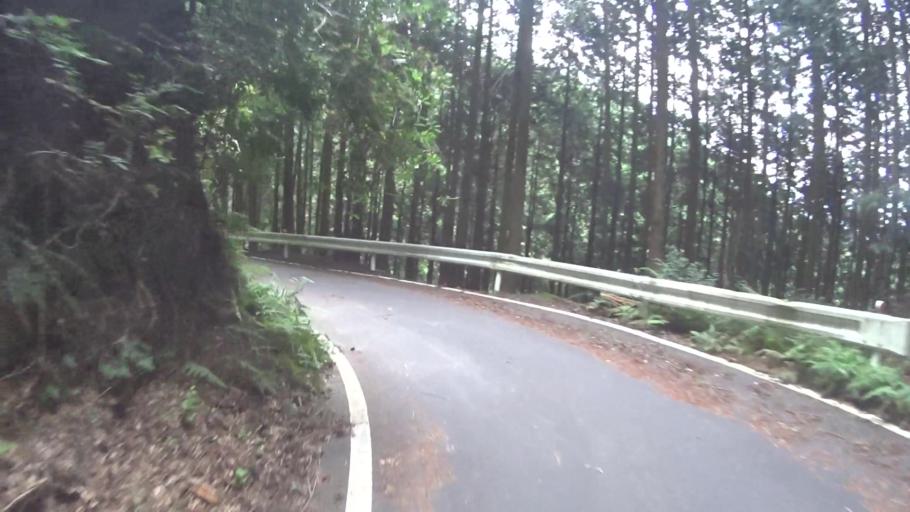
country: JP
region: Kyoto
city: Uji
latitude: 34.8485
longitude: 135.9420
